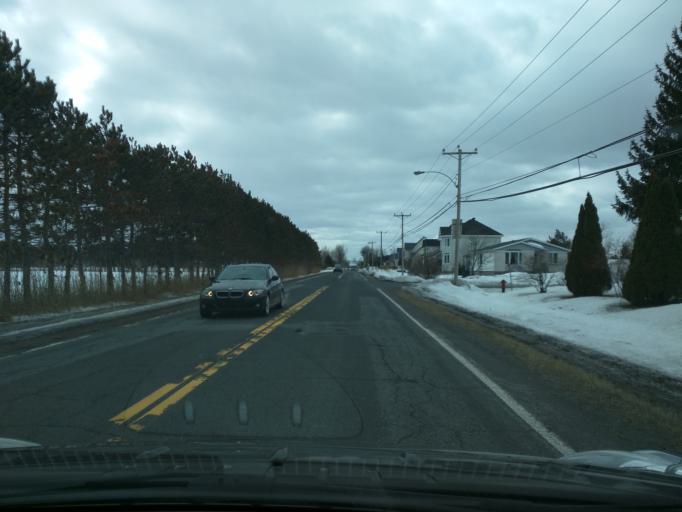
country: CA
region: Quebec
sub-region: Monteregie
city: Sainte-Julie
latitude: 45.6775
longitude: -73.2670
